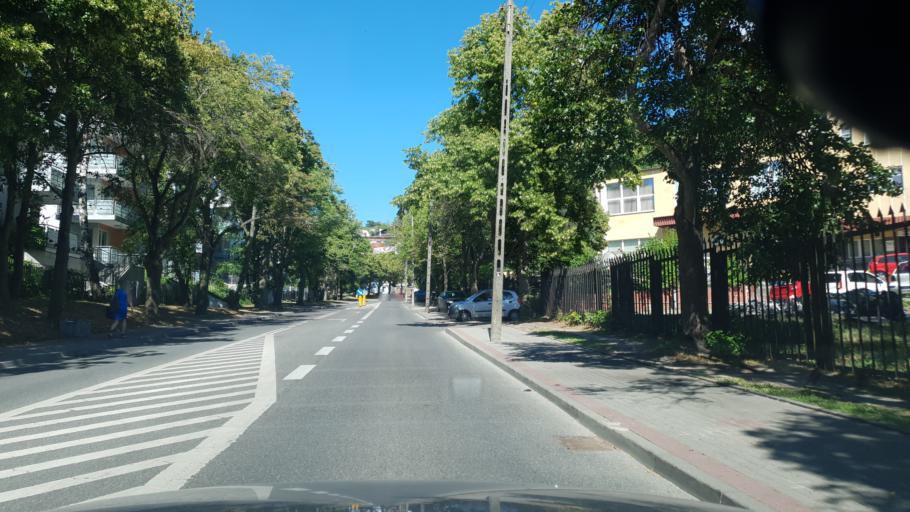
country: PL
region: Pomeranian Voivodeship
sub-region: Gdynia
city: Gdynia
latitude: 54.4886
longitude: 18.5493
